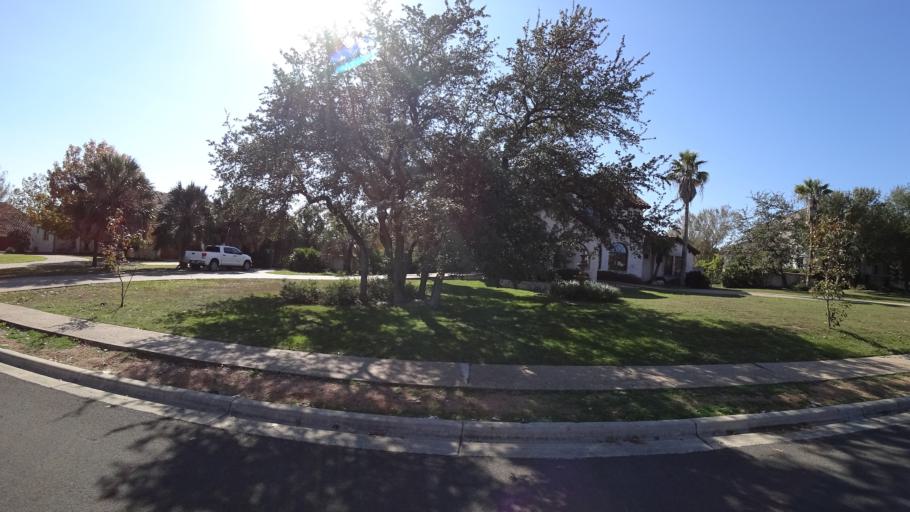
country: US
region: Texas
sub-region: Williamson County
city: Anderson Mill
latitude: 30.3813
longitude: -97.8494
